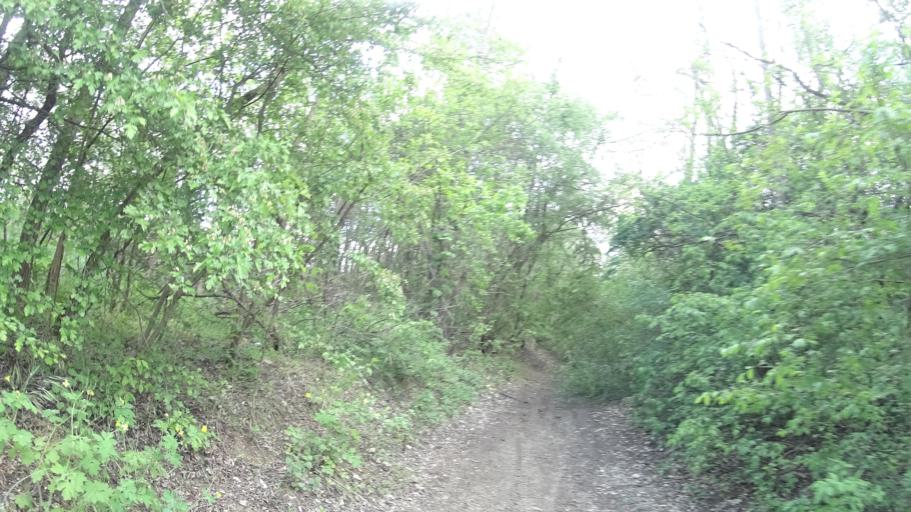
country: HU
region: Komarom-Esztergom
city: Dorog
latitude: 47.7142
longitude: 18.7601
